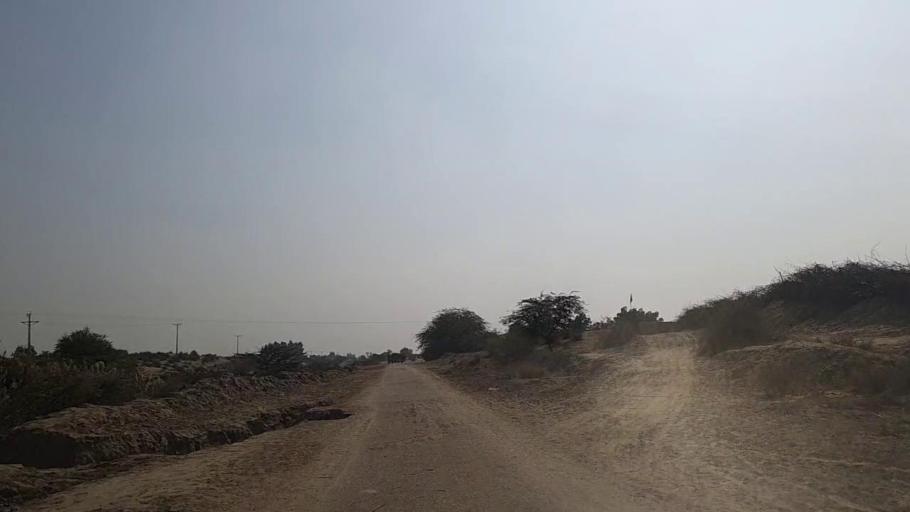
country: PK
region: Sindh
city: Daur
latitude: 26.4656
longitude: 68.4671
